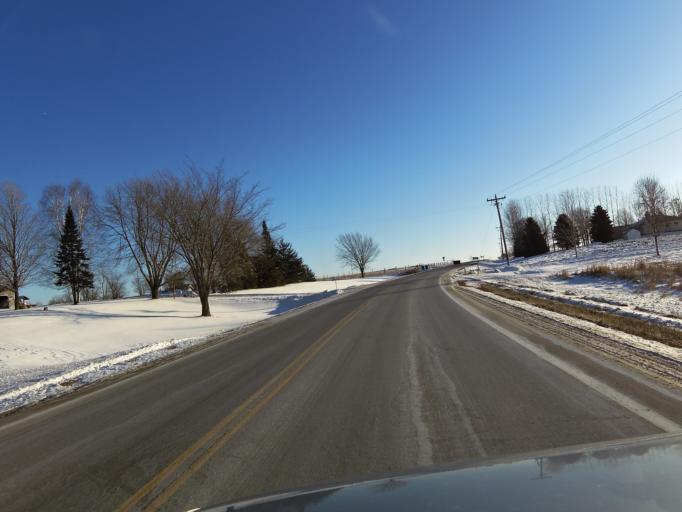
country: US
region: Minnesota
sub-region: Carver County
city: Carver
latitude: 44.7327
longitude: -93.5740
